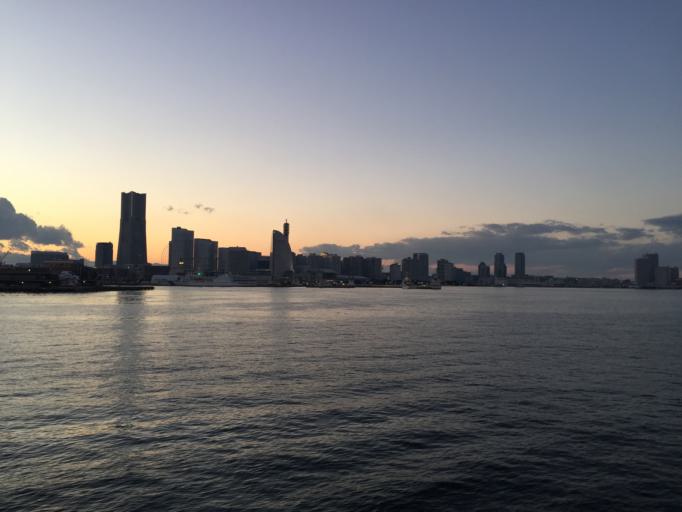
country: JP
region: Kanagawa
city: Yokohama
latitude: 35.4532
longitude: 139.6542
